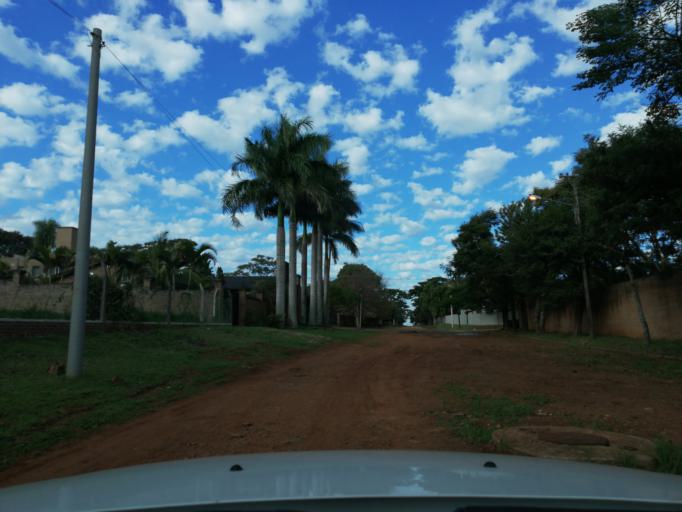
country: AR
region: Misiones
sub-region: Departamento de Capital
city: Posadas
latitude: -27.3560
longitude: -55.9340
